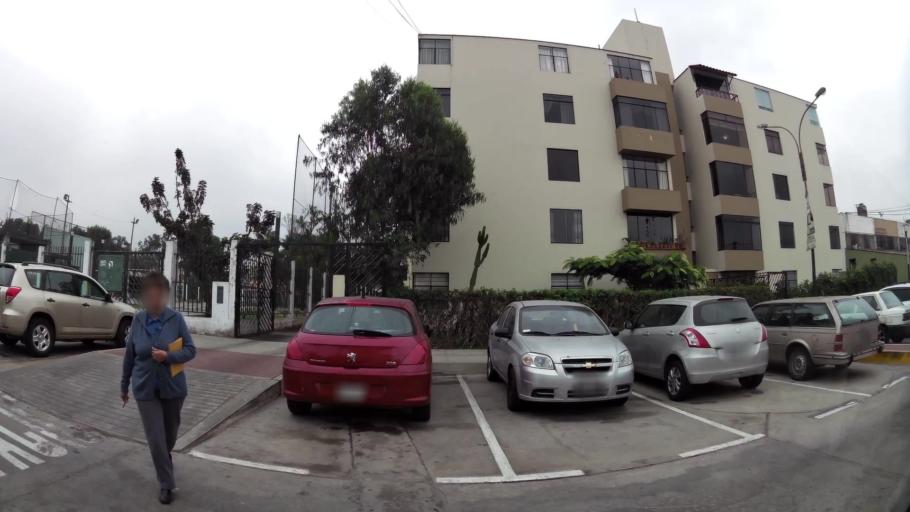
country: PE
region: Lima
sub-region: Lima
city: Surco
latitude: -12.1374
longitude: -77.0015
